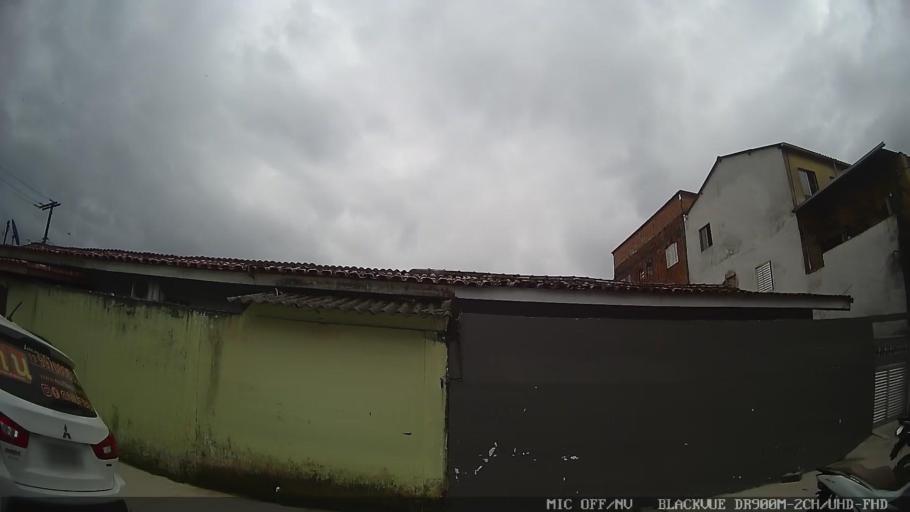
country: BR
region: Sao Paulo
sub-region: Guaruja
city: Guaruja
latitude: -23.9966
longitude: -46.2857
